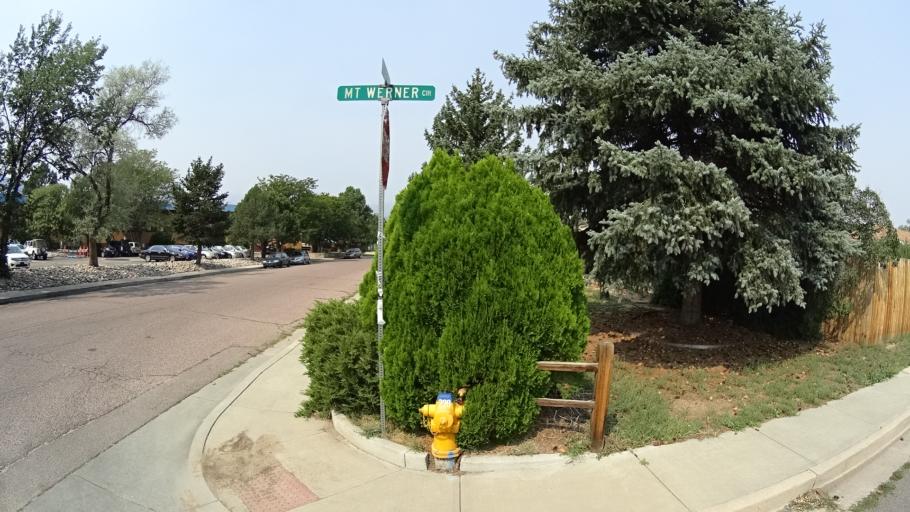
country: US
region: Colorado
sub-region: El Paso County
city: Colorado Springs
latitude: 38.8025
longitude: -104.8102
